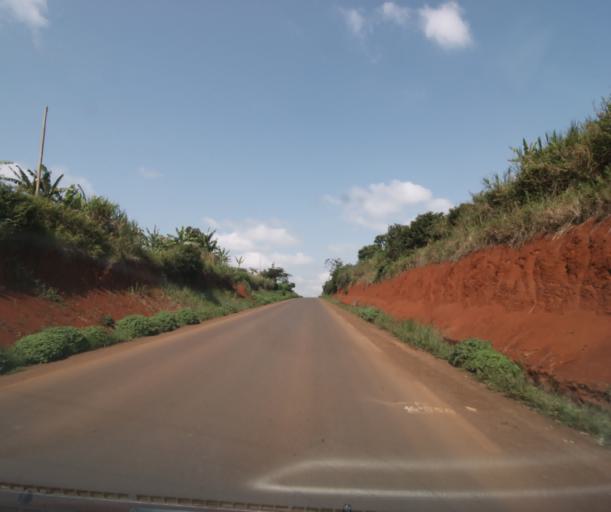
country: CM
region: West
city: Bansoa
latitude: 5.4970
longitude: 10.2304
